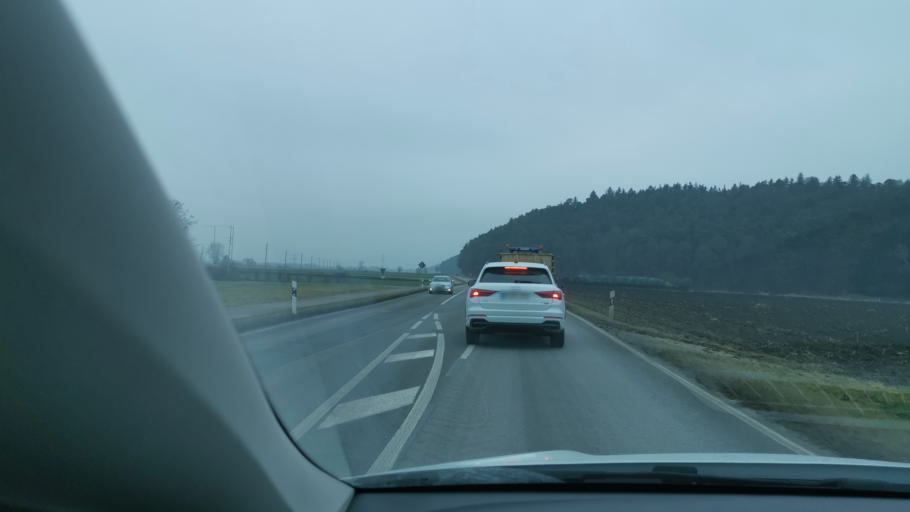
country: DE
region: Bavaria
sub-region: Swabia
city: Todtenweis
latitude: 48.5188
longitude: 10.9169
